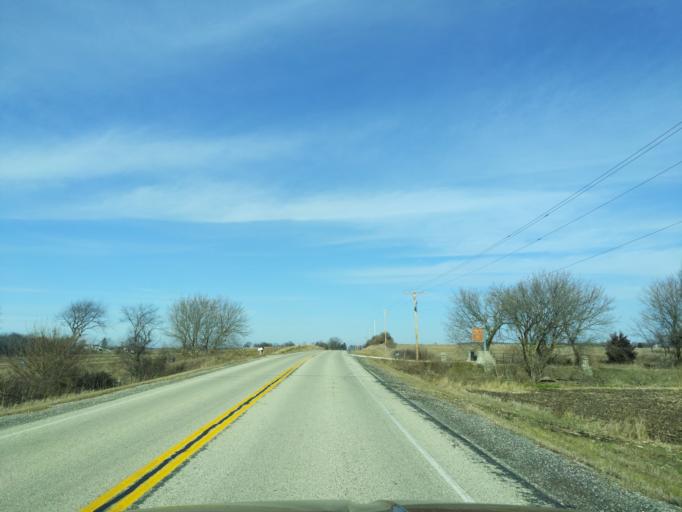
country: US
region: Wisconsin
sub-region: Jefferson County
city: Palmyra
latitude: 42.7696
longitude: -88.6031
